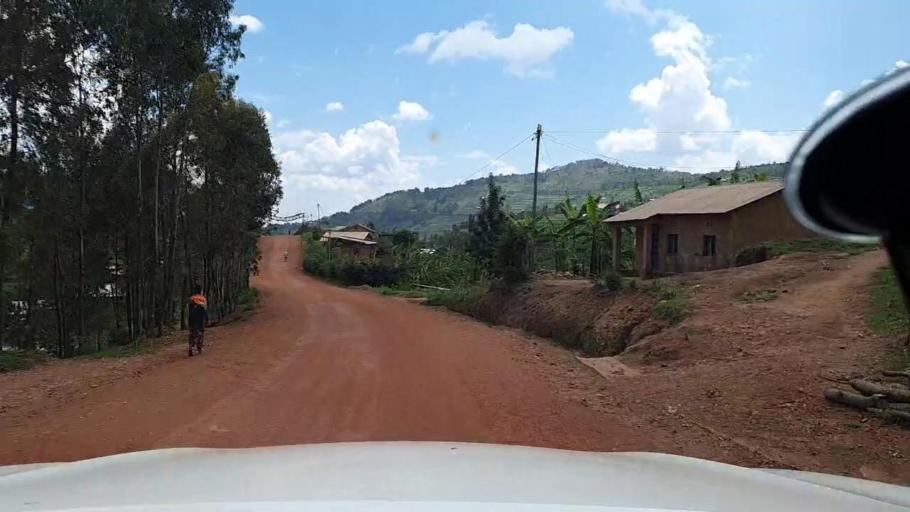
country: RW
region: Kigali
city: Kigali
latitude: -1.7692
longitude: 29.8417
